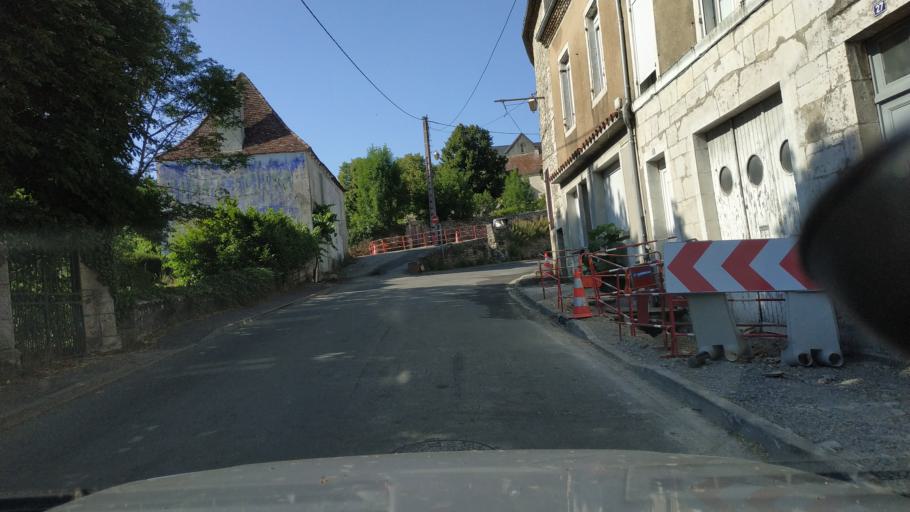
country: FR
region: Midi-Pyrenees
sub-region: Departement du Lot
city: Gramat
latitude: 44.7770
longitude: 1.7234
